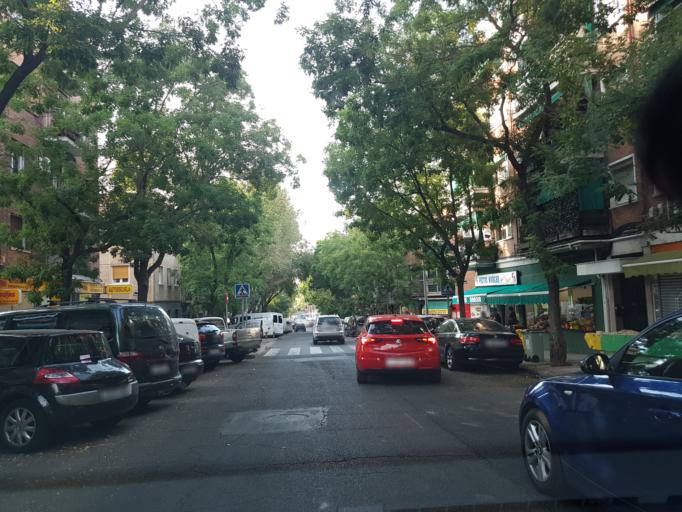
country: ES
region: Madrid
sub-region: Provincia de Madrid
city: Ciudad Lineal
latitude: 40.4367
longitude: -3.6455
